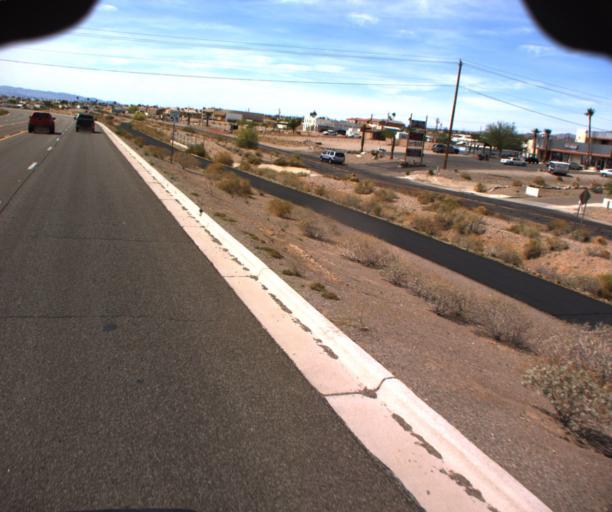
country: US
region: Arizona
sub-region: Mohave County
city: Lake Havasu City
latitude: 34.4540
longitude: -114.2671
